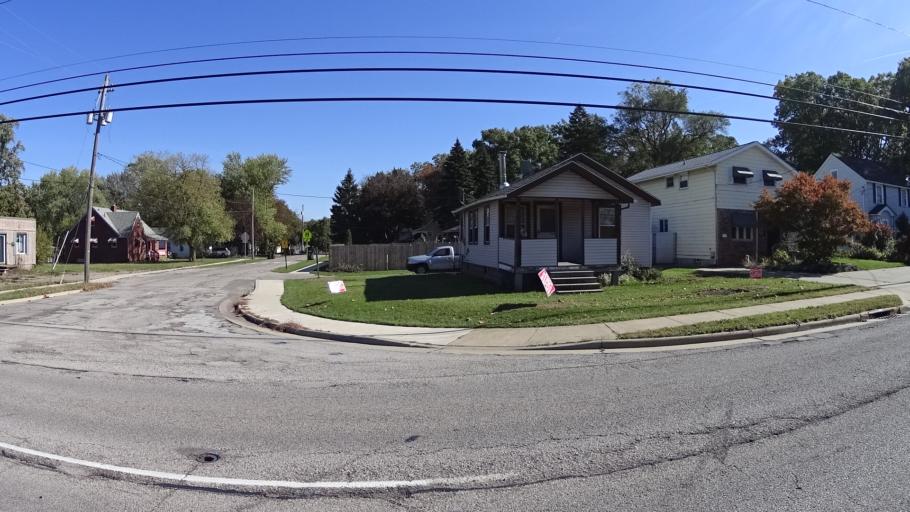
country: US
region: Ohio
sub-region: Lorain County
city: Lorain
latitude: 41.4270
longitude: -82.1626
